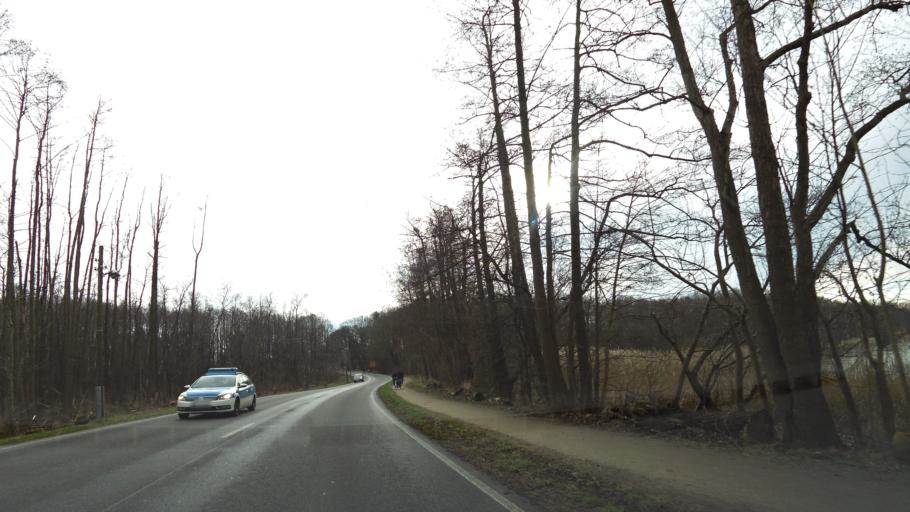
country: DE
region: Brandenburg
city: Strausberg
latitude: 52.5912
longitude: 13.8930
